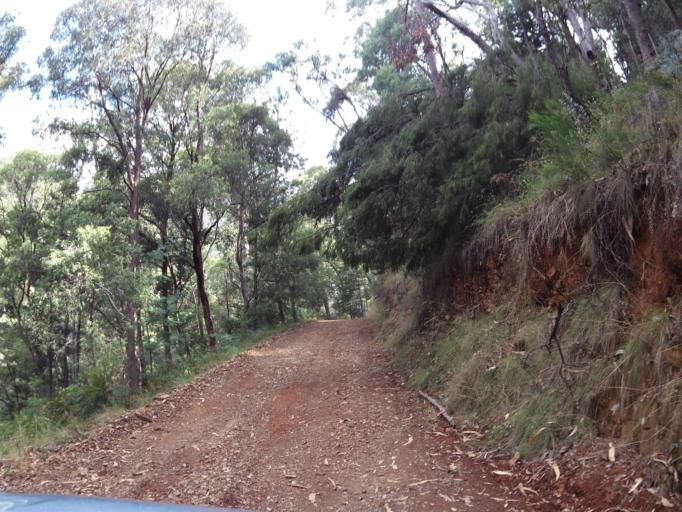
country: AU
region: Victoria
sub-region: Alpine
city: Mount Beauty
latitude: -36.7725
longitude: 147.0141
